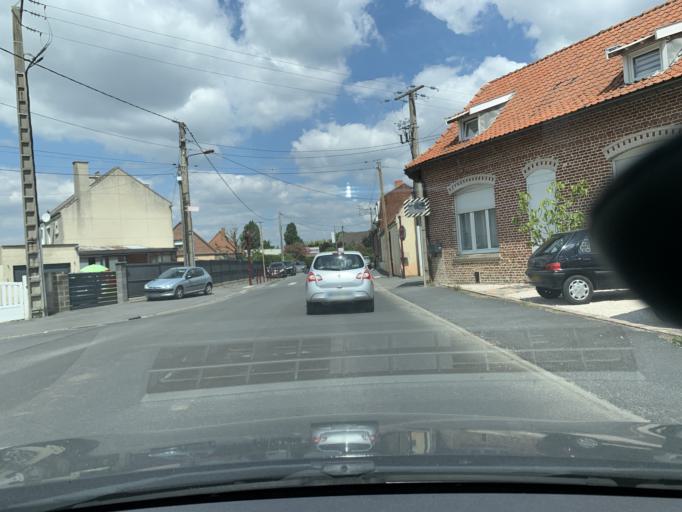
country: FR
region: Nord-Pas-de-Calais
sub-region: Departement du Nord
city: Goeulzin
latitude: 50.3210
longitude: 3.0952
